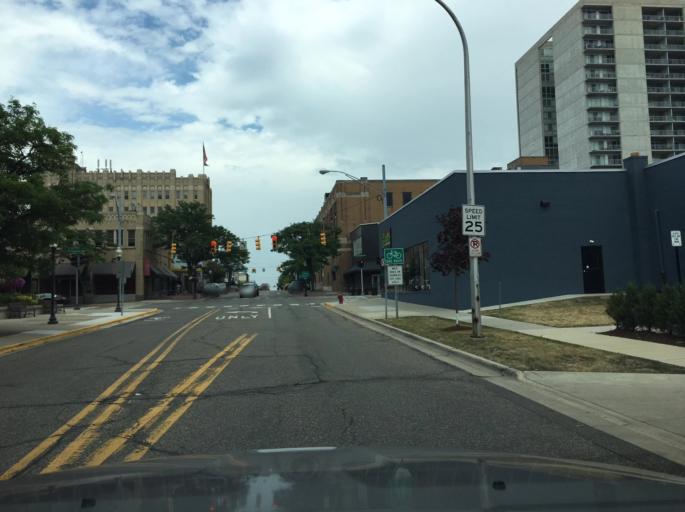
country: US
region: Michigan
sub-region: Oakland County
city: Royal Oak
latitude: 42.4872
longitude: -83.1485
